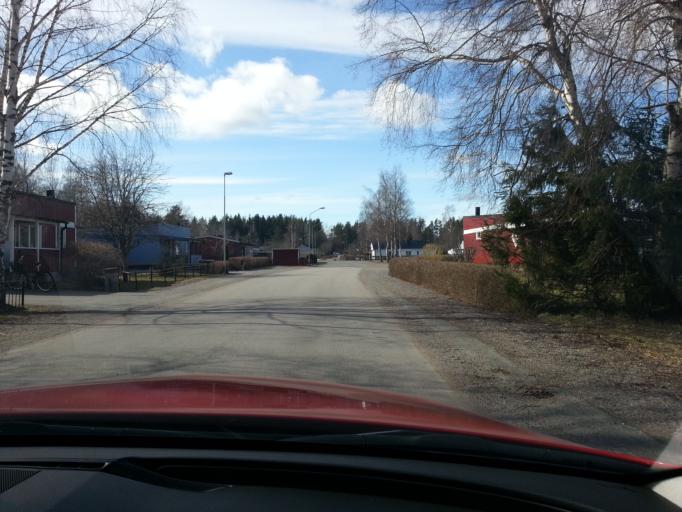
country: SE
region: Uppsala
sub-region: Osthammars Kommun
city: Gimo
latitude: 60.1658
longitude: 18.1789
